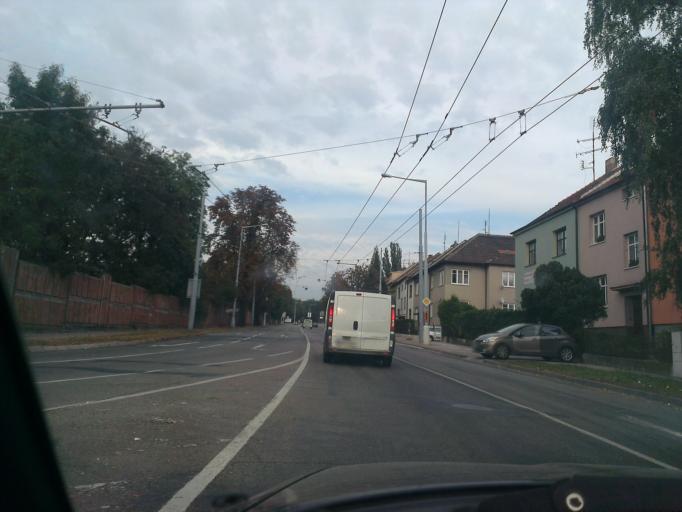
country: CZ
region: South Moravian
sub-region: Mesto Brno
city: Brno
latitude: 49.2057
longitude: 16.6421
